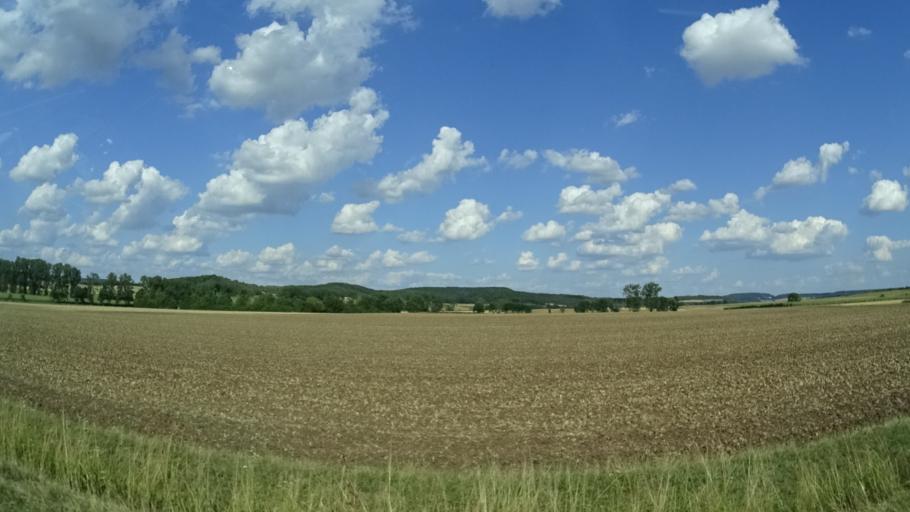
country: DE
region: Bavaria
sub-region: Regierungsbezirk Unterfranken
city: Bad Konigshofen im Grabfeld
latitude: 50.2891
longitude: 10.4871
